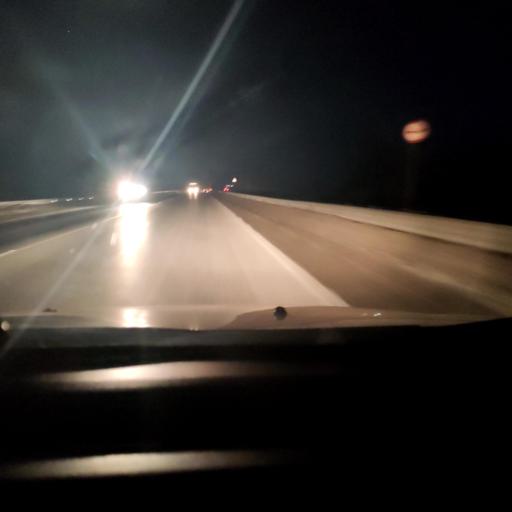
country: RU
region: Samara
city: Kinel'
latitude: 53.1896
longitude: 50.5151
